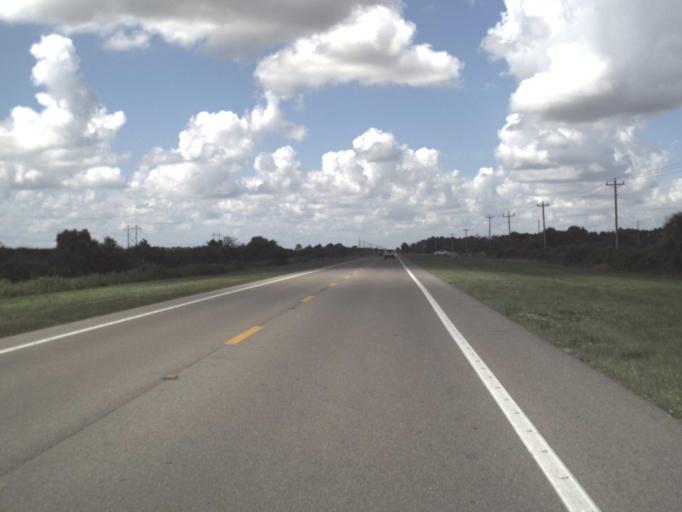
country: US
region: Florida
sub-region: Lee County
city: Lehigh Acres
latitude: 26.5239
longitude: -81.5850
